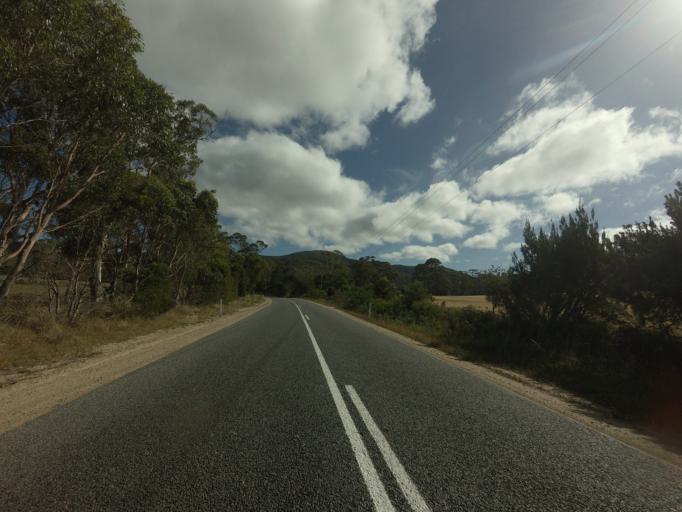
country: AU
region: Tasmania
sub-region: Break O'Day
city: St Helens
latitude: -41.7779
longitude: 148.2585
